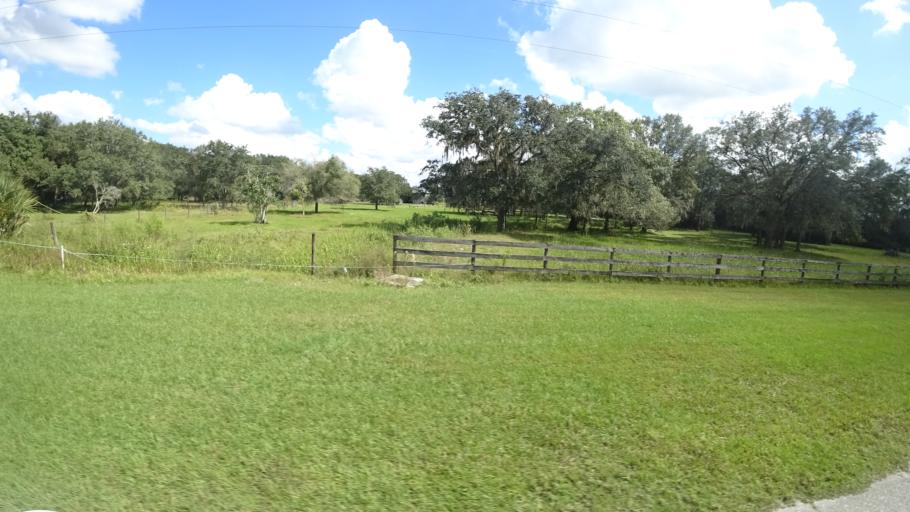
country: US
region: Florida
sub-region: Sarasota County
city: Lake Sarasota
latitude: 27.2849
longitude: -82.2231
